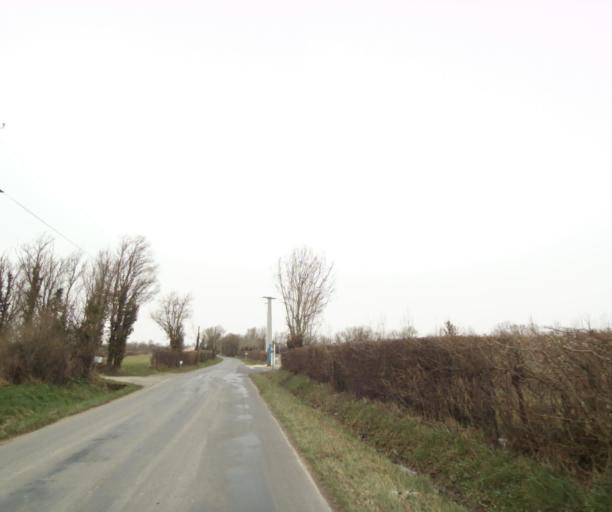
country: FR
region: Poitou-Charentes
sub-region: Departement des Deux-Sevres
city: Niort
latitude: 46.3054
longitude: -0.4762
